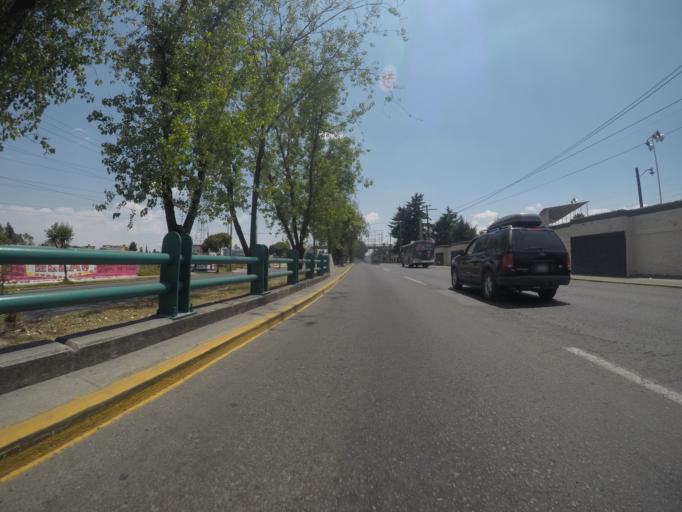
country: MX
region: Mexico
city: Toluca
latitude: 19.2823
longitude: -99.6316
